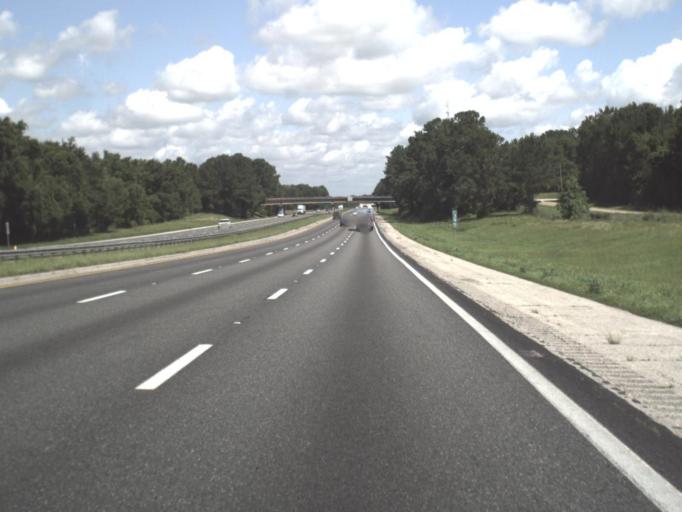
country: US
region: Florida
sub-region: Alachua County
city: Alachua
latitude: 29.7504
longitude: -82.4900
